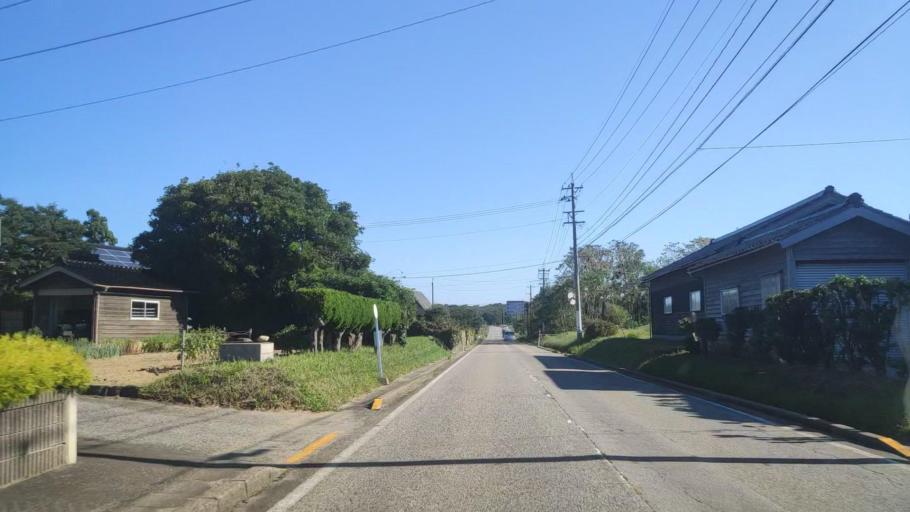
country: JP
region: Ishikawa
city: Hakui
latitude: 36.9574
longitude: 136.7707
